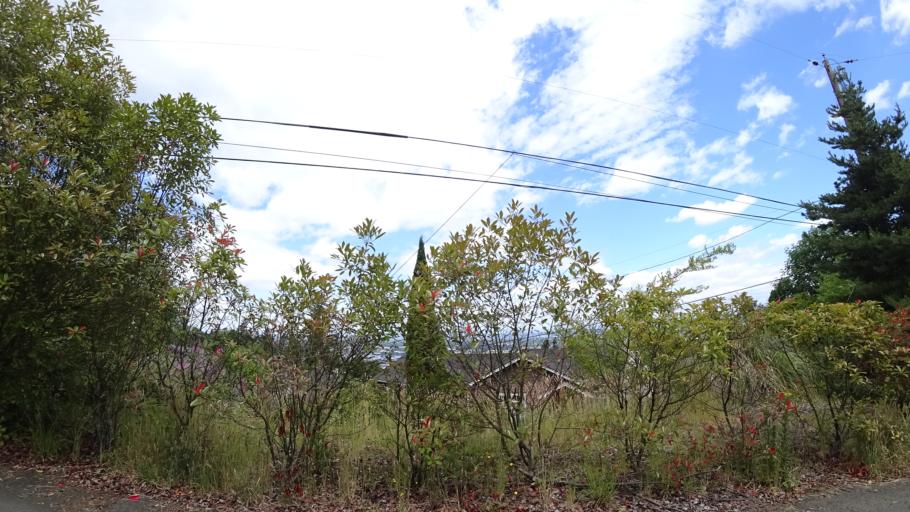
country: US
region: Oregon
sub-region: Multnomah County
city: Portland
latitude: 45.5264
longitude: -122.7102
